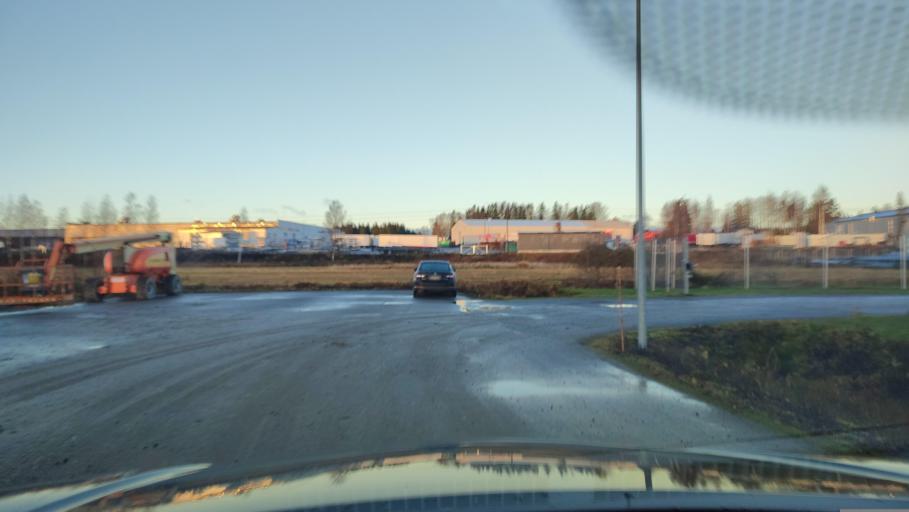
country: FI
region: Ostrobothnia
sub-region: Sydosterbotten
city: Naerpes
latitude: 62.4760
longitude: 21.3760
